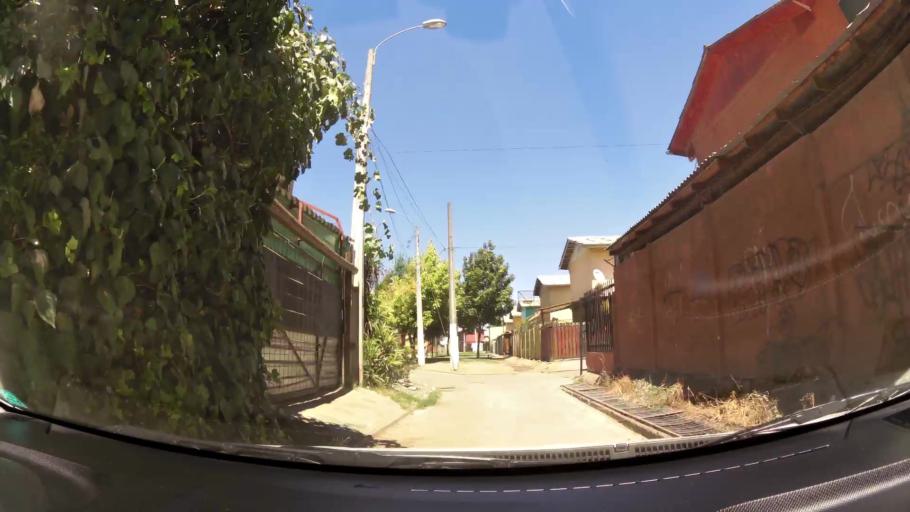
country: CL
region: O'Higgins
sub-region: Provincia de Cachapoal
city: Rancagua
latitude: -34.1546
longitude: -70.7493
